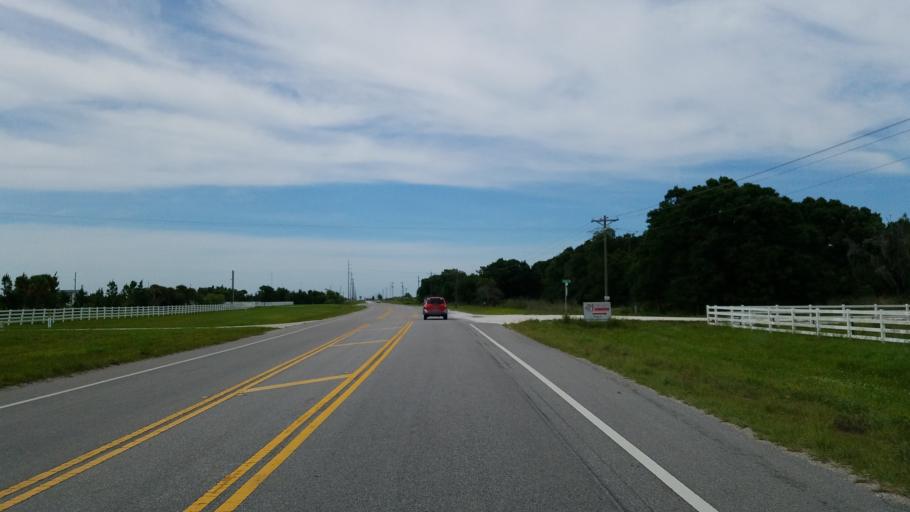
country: US
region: Florida
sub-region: Hillsborough County
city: Balm
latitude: 27.6426
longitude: -82.1464
